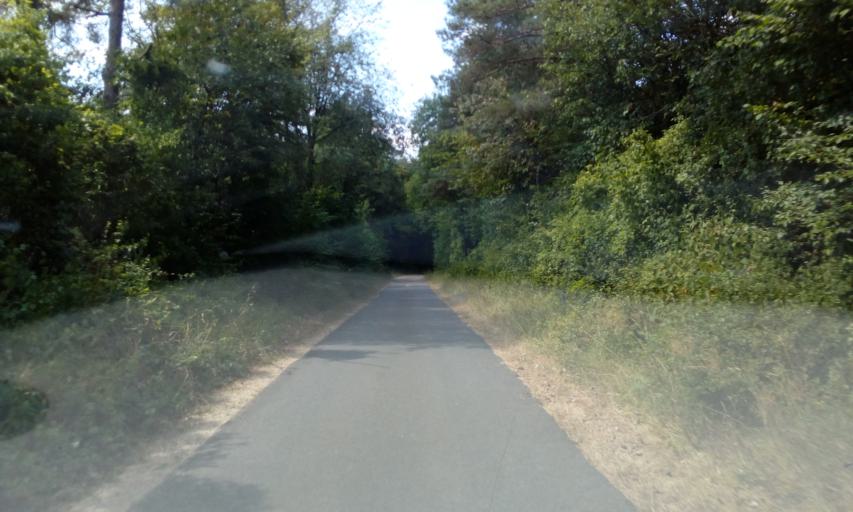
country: FR
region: Lorraine
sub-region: Departement de Meurthe-et-Moselle
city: Pagny-sur-Moselle
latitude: 48.9507
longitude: 5.9101
